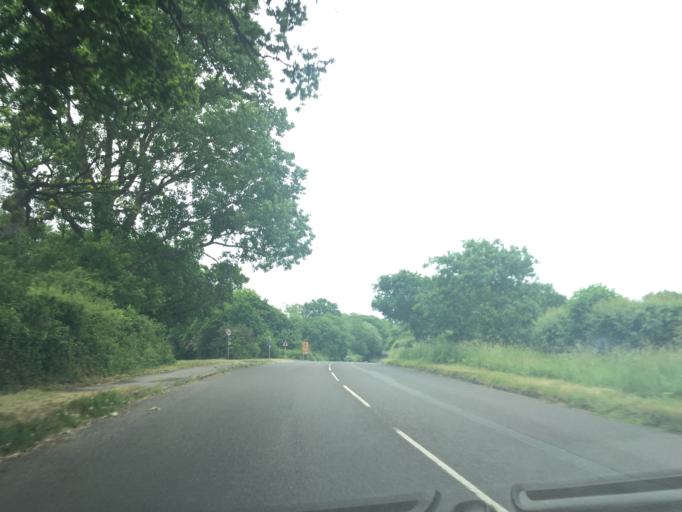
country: GB
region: England
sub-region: Dorset
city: Bovington Camp
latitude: 50.6916
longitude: -2.2276
